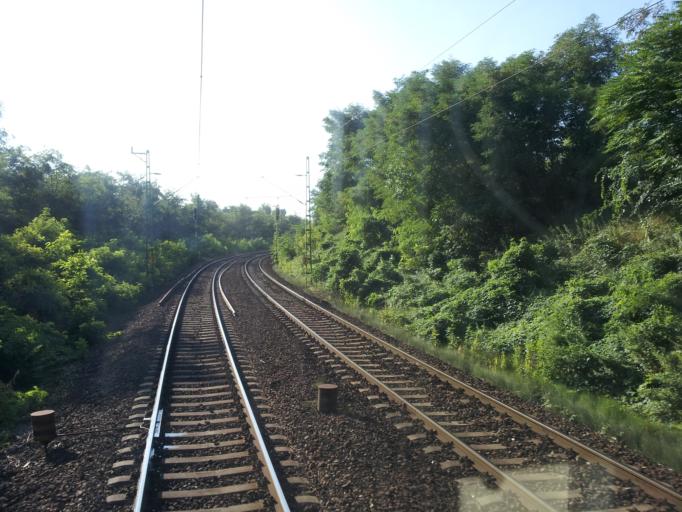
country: HU
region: Budapest
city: Budapest XIV. keruelet
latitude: 47.4881
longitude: 19.1165
